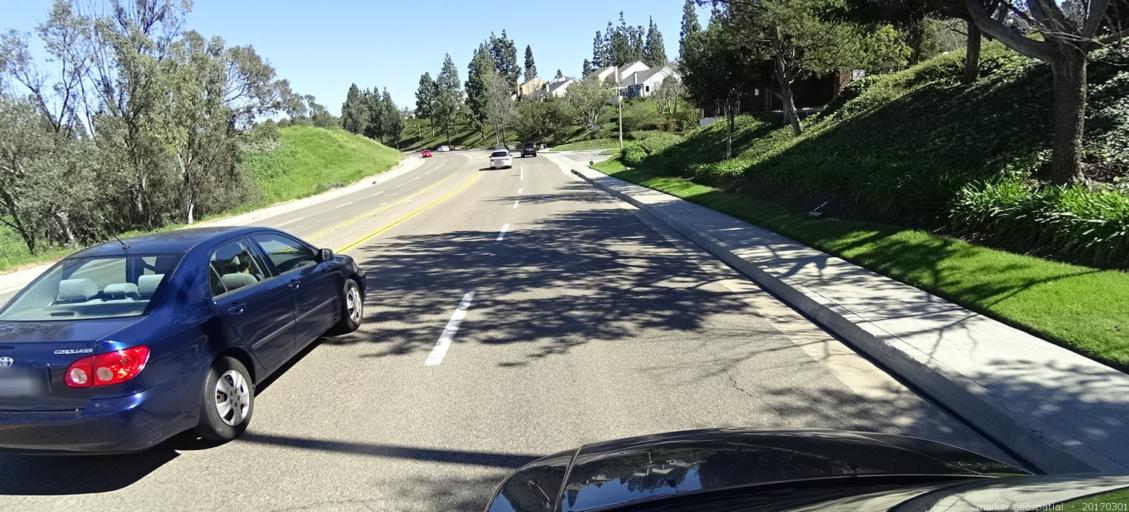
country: US
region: California
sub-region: Orange County
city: Villa Park
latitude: 33.8450
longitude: -117.7833
